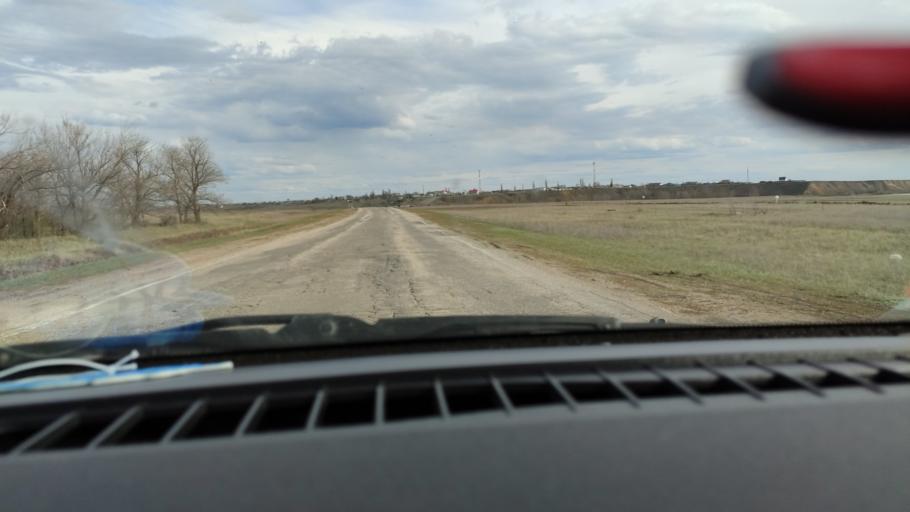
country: RU
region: Saratov
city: Rovnoye
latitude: 51.0320
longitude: 46.0871
